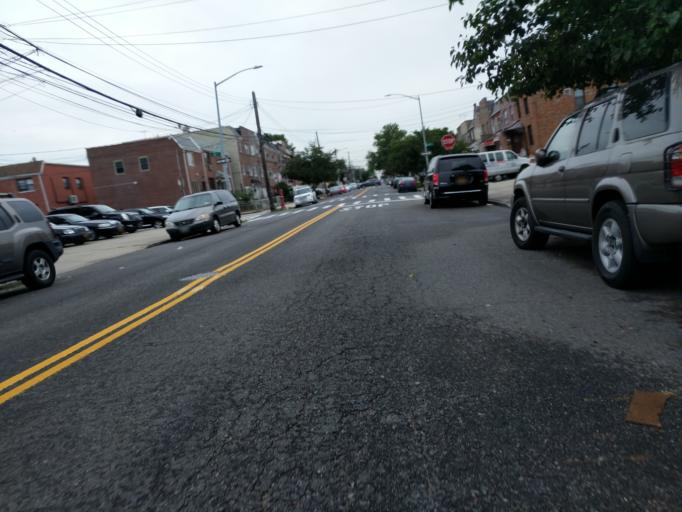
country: US
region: New York
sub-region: Queens County
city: Long Island City
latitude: 40.7620
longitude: -73.9061
